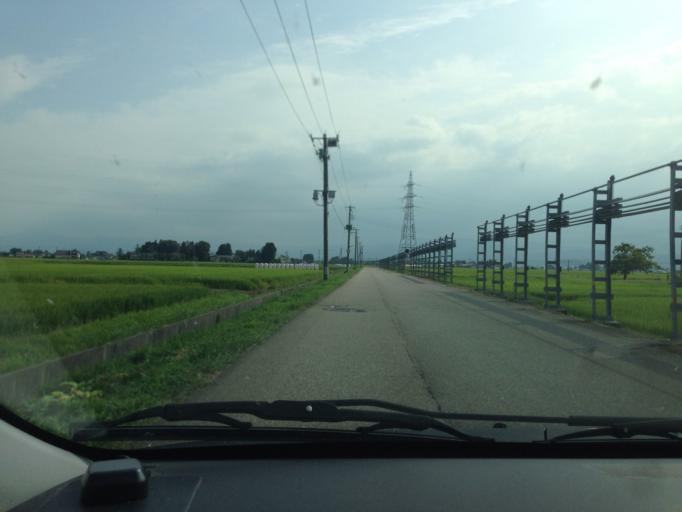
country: JP
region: Fukushima
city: Kitakata
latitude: 37.5770
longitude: 139.8550
